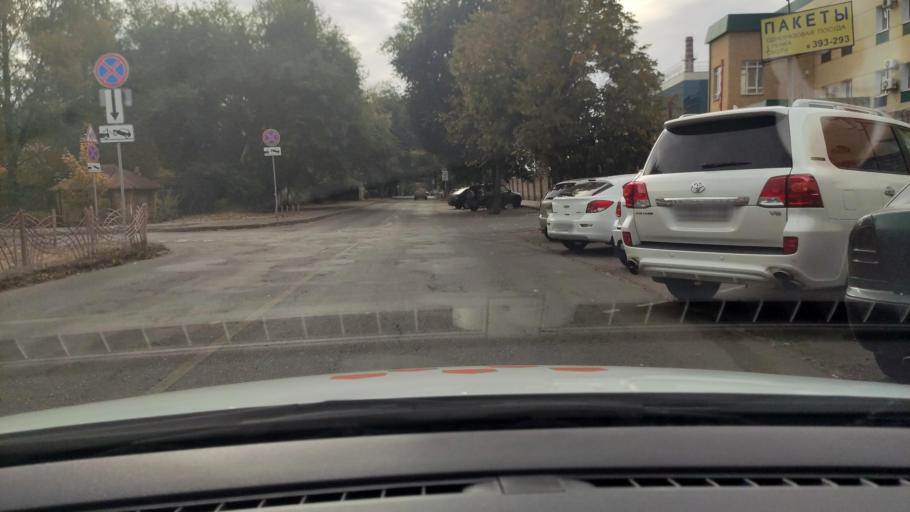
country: RU
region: Voronezj
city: Voronezh
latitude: 51.6625
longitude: 39.1825
